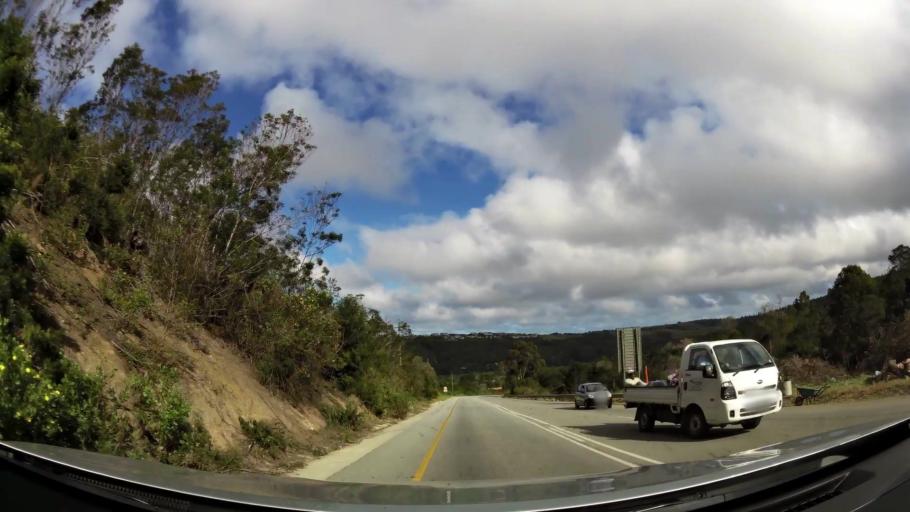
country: ZA
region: Western Cape
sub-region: Eden District Municipality
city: Plettenberg Bay
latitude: -34.0553
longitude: 23.3547
